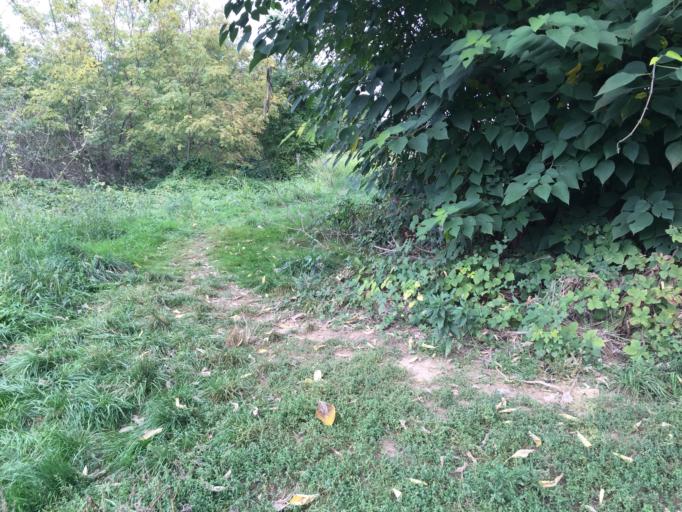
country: IT
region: Piedmont
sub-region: Provincia di Torino
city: Trofarello
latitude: 44.9932
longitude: 7.7402
